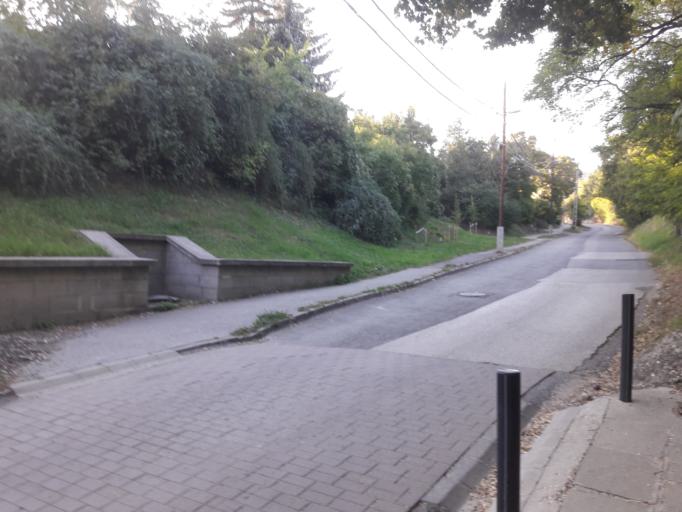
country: HU
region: Pest
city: Budaors
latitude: 47.4786
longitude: 18.9838
